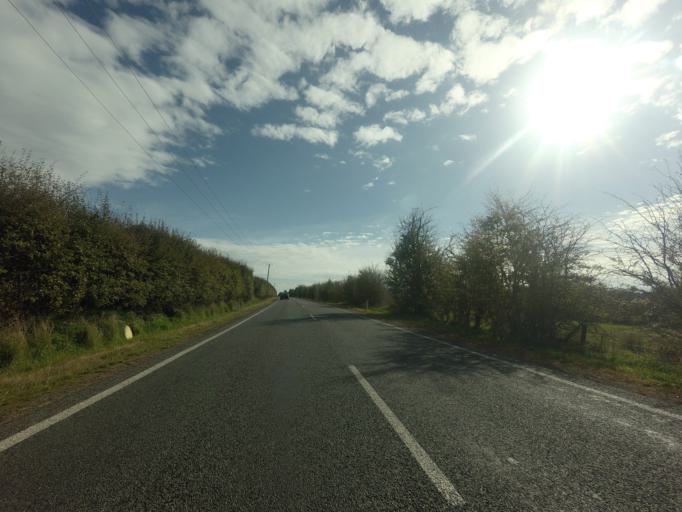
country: AU
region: Tasmania
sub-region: Meander Valley
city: Westbury
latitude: -41.5249
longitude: 146.7859
